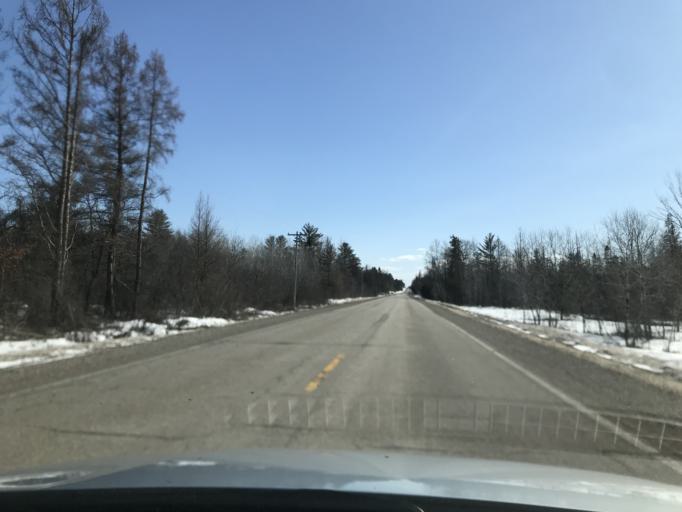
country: US
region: Wisconsin
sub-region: Marinette County
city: Niagara
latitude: 45.3738
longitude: -88.1001
